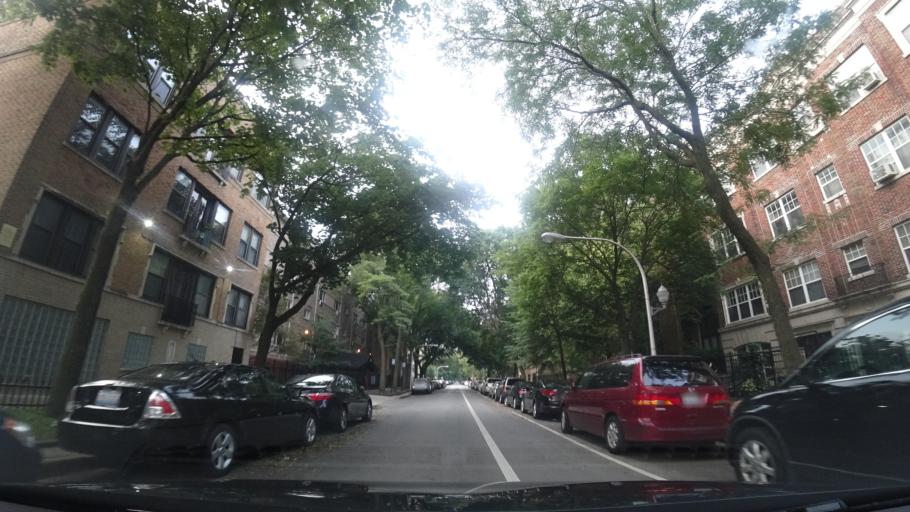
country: US
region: Illinois
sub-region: Cook County
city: Evanston
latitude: 41.9830
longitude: -87.6580
